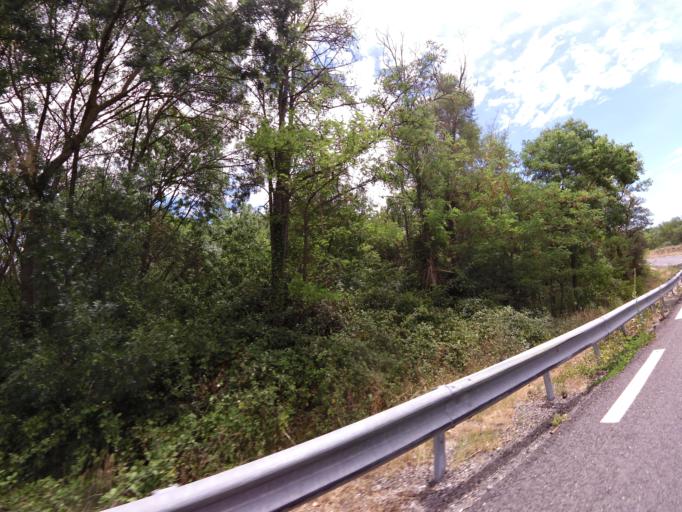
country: FR
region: Languedoc-Roussillon
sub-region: Departement du Gard
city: Quissac
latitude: 43.8813
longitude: 4.0072
